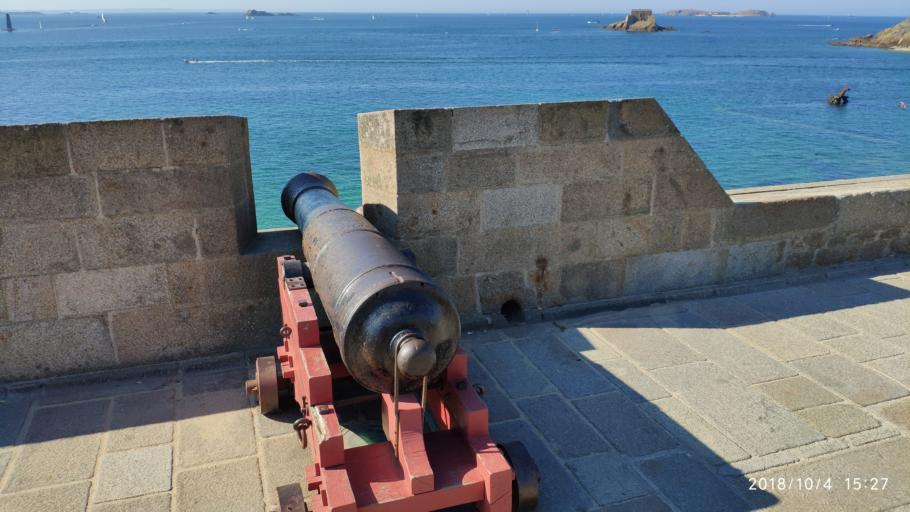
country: FR
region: Brittany
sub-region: Departement d'Ille-et-Vilaine
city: Saint-Malo
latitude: 48.6471
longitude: -2.0290
